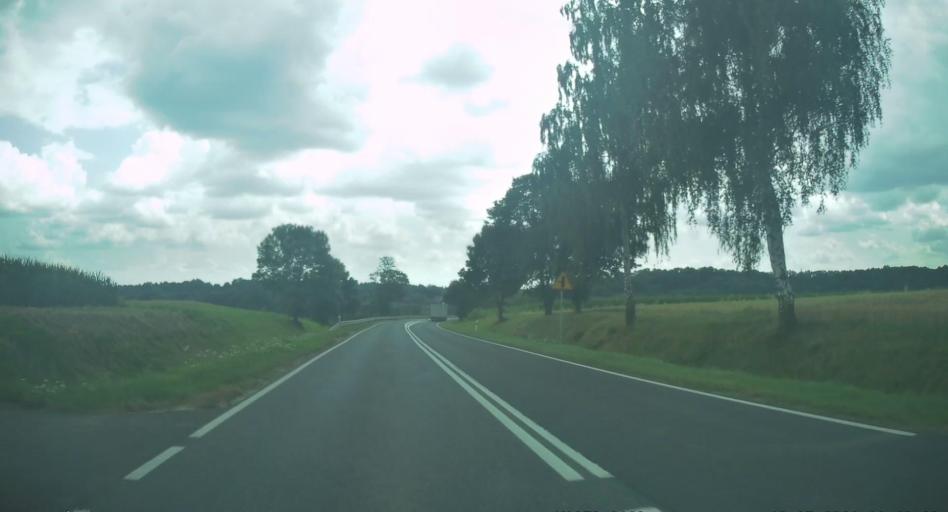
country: PL
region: Opole Voivodeship
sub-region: Powiat prudnicki
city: Laka Prudnicka
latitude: 50.4093
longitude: 17.5061
